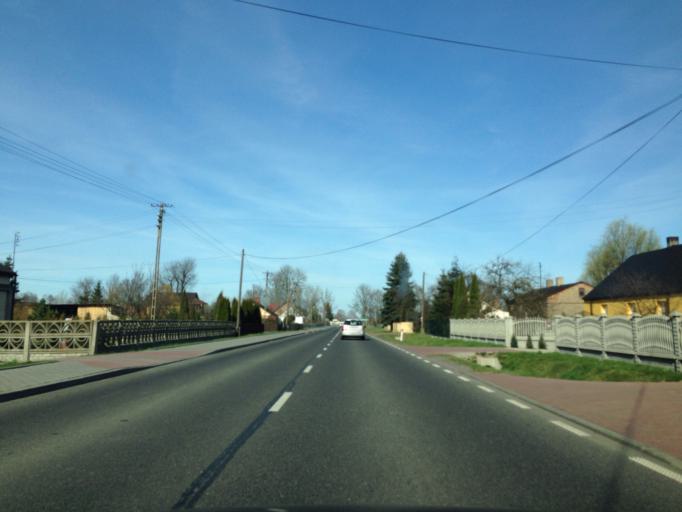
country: PL
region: Lodz Voivodeship
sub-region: Powiat poddebicki
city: Wartkowice
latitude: 52.0060
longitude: 19.0705
